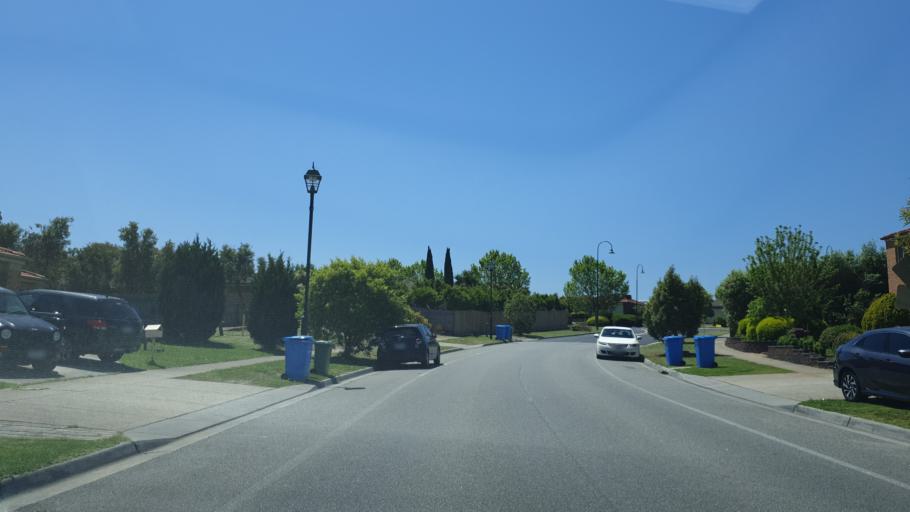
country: AU
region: Victoria
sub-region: Casey
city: Narre Warren South
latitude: -38.0631
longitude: 145.2918
